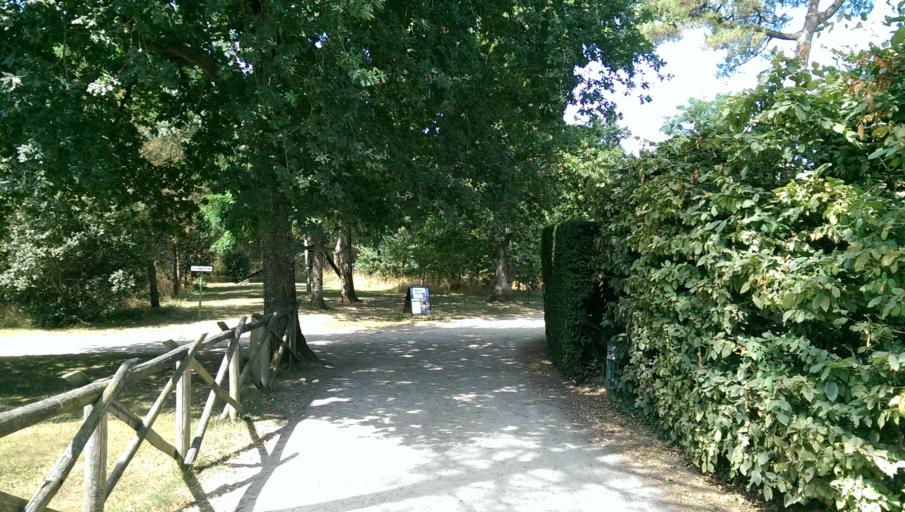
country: FR
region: Pays de la Loire
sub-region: Departement de la Loire-Atlantique
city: Clisson
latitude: 47.0859
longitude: -1.2717
